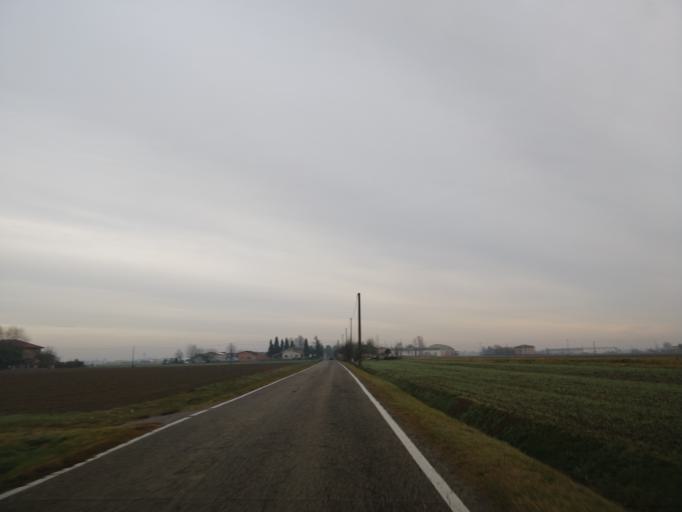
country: IT
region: Emilia-Romagna
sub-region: Provincia di Ferrara
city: Dosso
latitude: 44.7809
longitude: 11.3345
